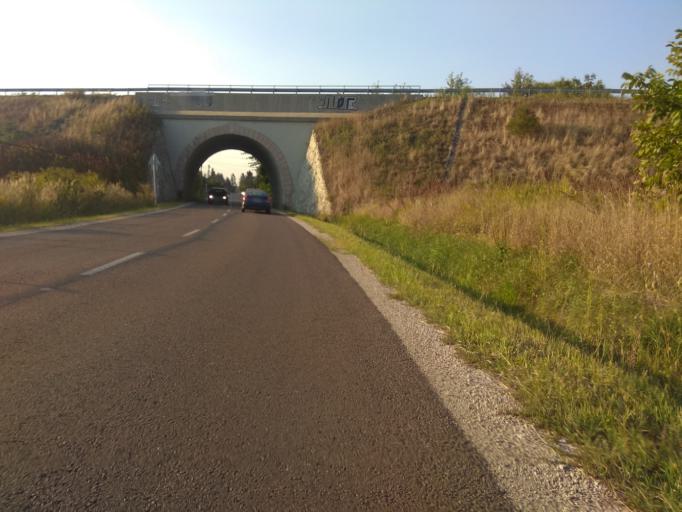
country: HU
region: Borsod-Abauj-Zemplen
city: Nyekladhaza
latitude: 47.9871
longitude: 20.8391
